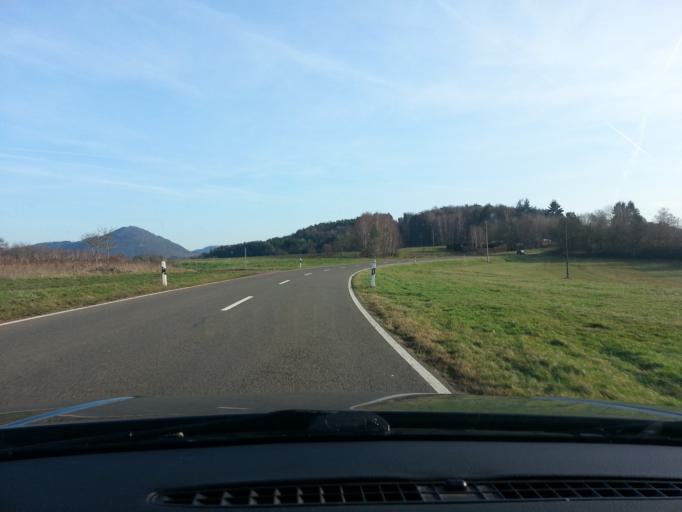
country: DE
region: Rheinland-Pfalz
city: Wernersberg
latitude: 49.1764
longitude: 7.9233
